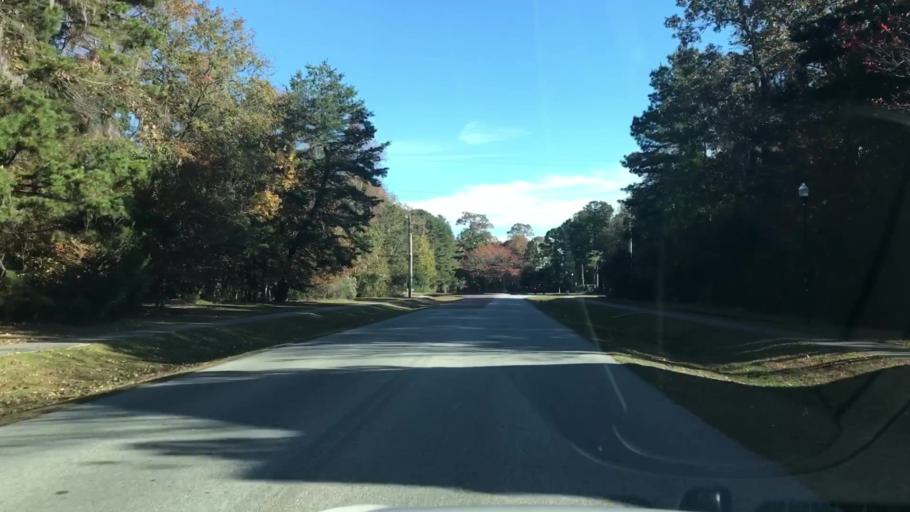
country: US
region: South Carolina
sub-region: Charleston County
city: Shell Point
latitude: 32.8369
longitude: -80.0894
